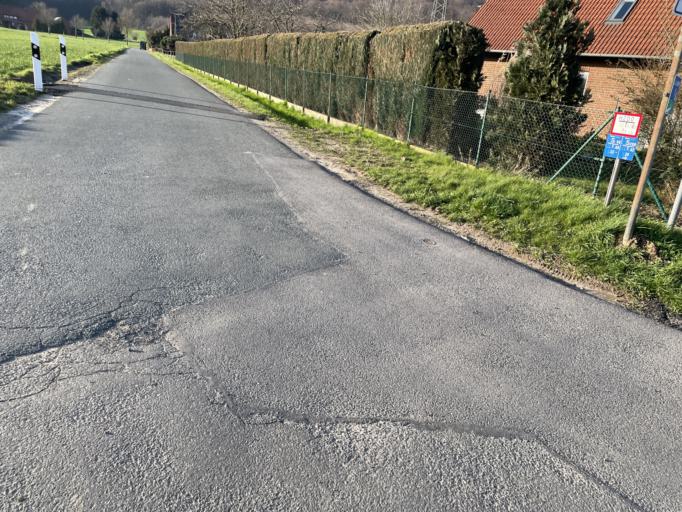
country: DE
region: North Rhine-Westphalia
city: Porta Westfalica
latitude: 52.2299
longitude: 8.9699
